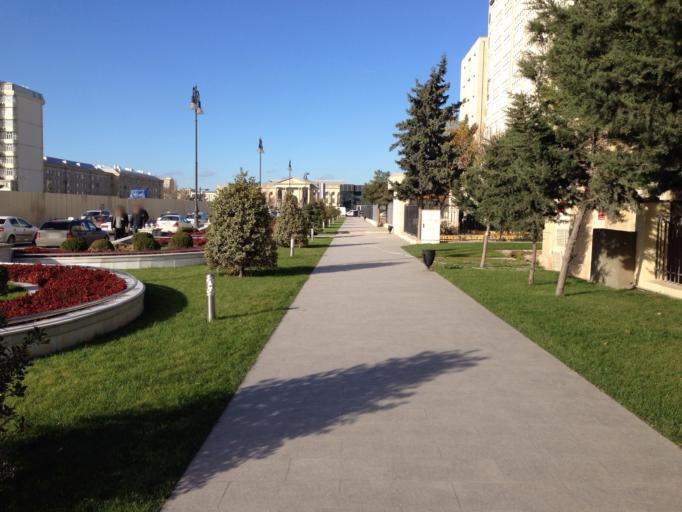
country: AZ
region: Baki
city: Baku
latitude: 40.4028
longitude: 49.8578
